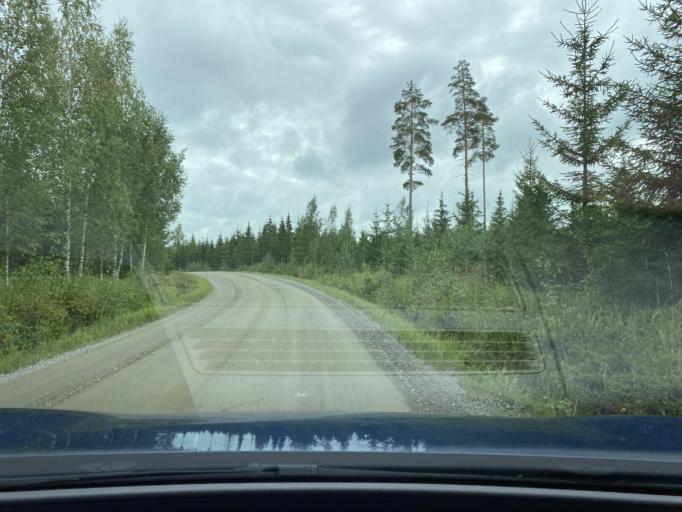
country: FI
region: Pirkanmaa
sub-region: Lounais-Pirkanmaa
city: Punkalaidun
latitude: 61.2111
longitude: 23.1708
